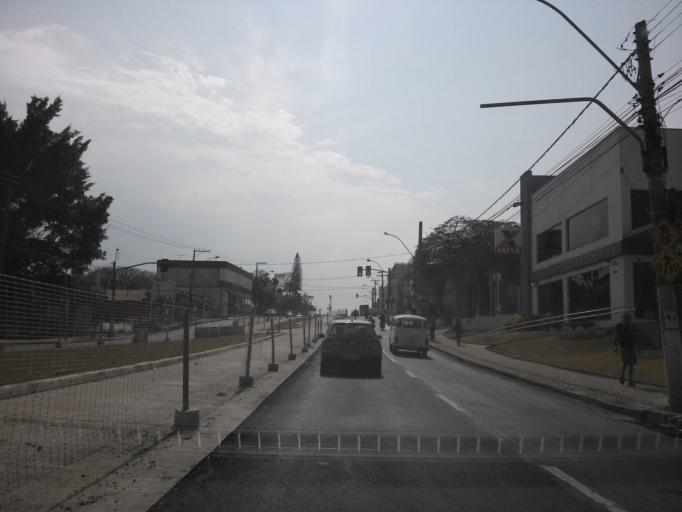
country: BR
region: Sao Paulo
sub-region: Campinas
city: Campinas
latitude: -22.9218
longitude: -47.0777
